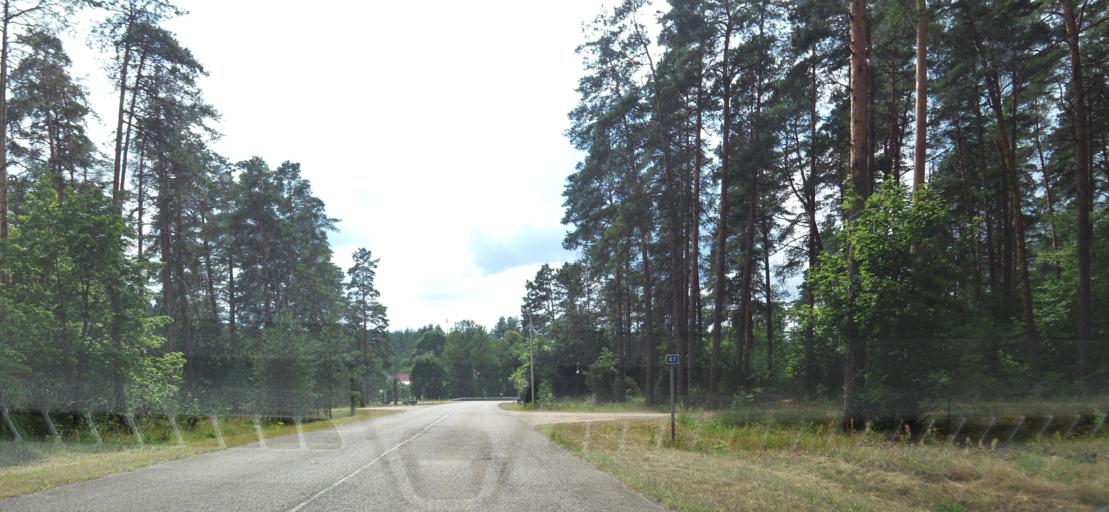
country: LT
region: Alytaus apskritis
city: Druskininkai
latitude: 53.9887
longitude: 24.1004
